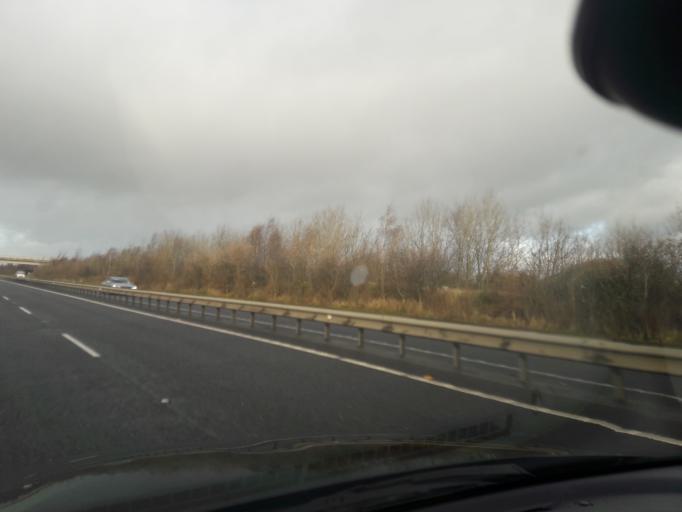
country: IE
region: Leinster
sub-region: An Mhi
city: Ashbourne
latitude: 53.4654
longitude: -6.3599
